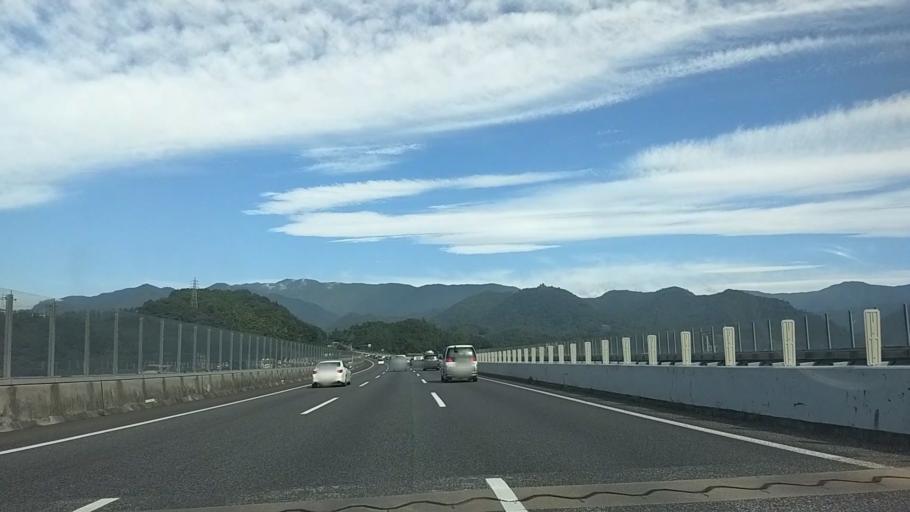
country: JP
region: Yamanashi
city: Uenohara
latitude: 35.6274
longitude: 139.1038
